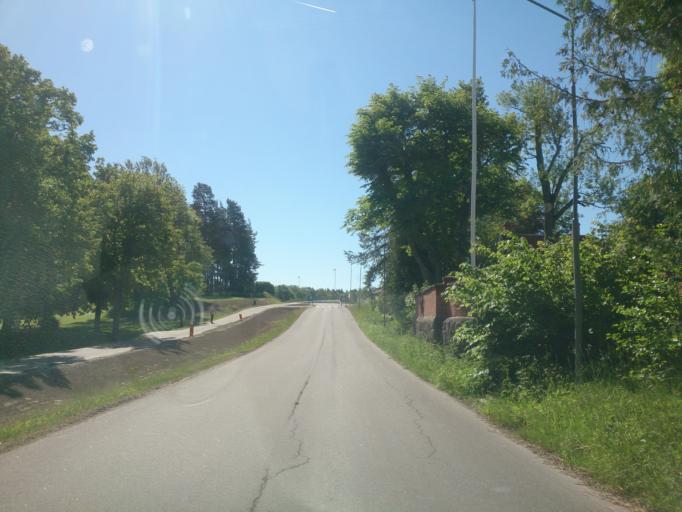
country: SE
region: OEstergoetland
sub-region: Atvidabergs Kommun
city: Atvidaberg
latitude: 58.1930
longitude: 15.9945
